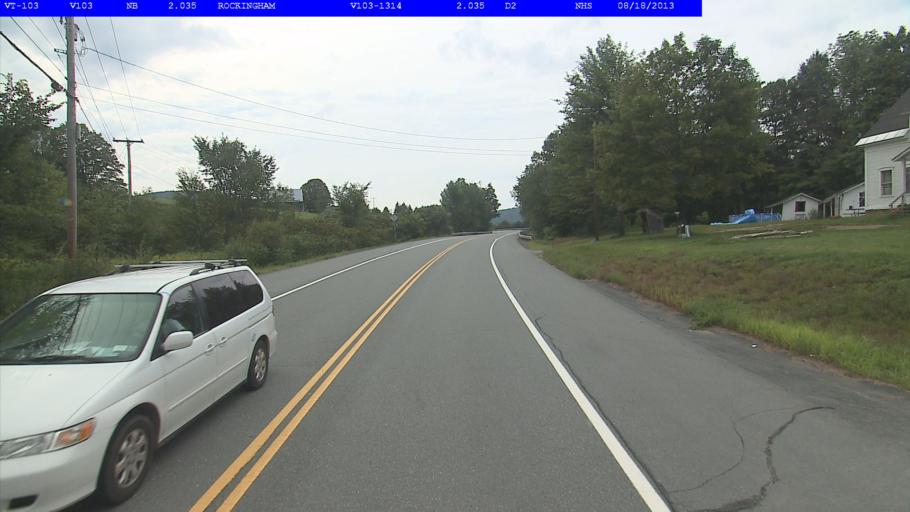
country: US
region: Vermont
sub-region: Windham County
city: Rockingham
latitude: 43.1928
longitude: -72.4933
